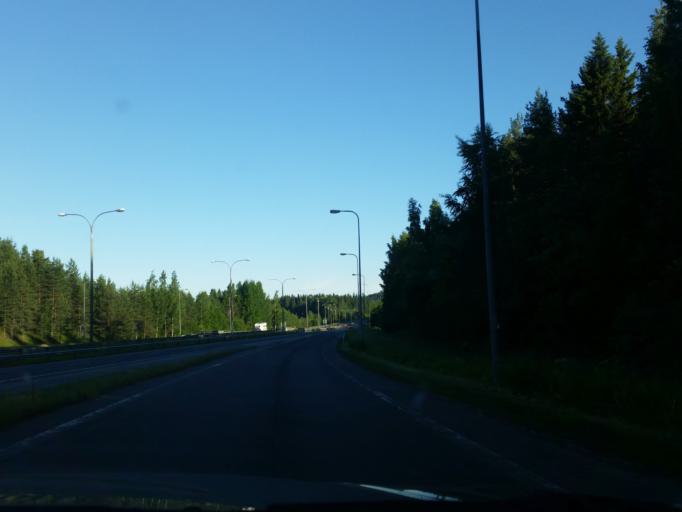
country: FI
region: Northern Savo
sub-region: Kuopio
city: Kuopio
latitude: 62.8608
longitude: 27.6181
